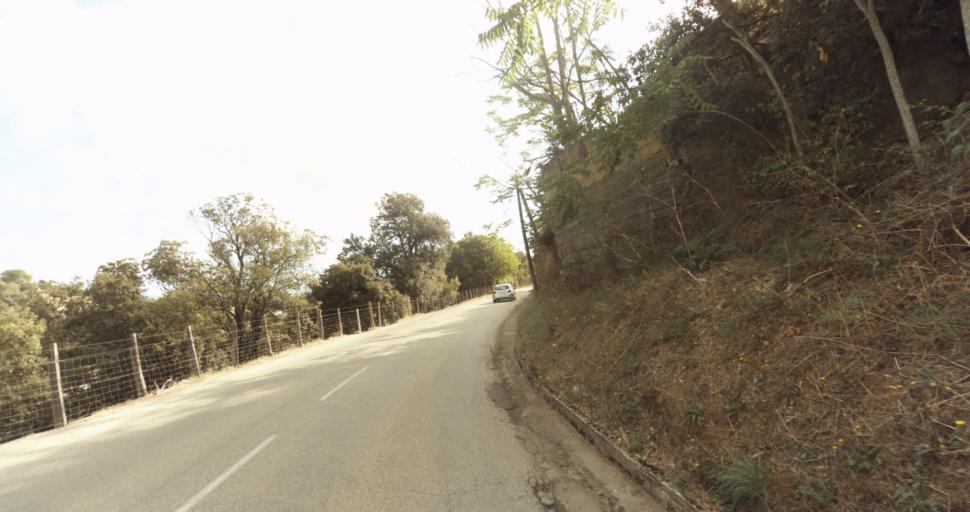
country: FR
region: Corsica
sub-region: Departement de la Corse-du-Sud
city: Ajaccio
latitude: 41.9308
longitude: 8.7160
